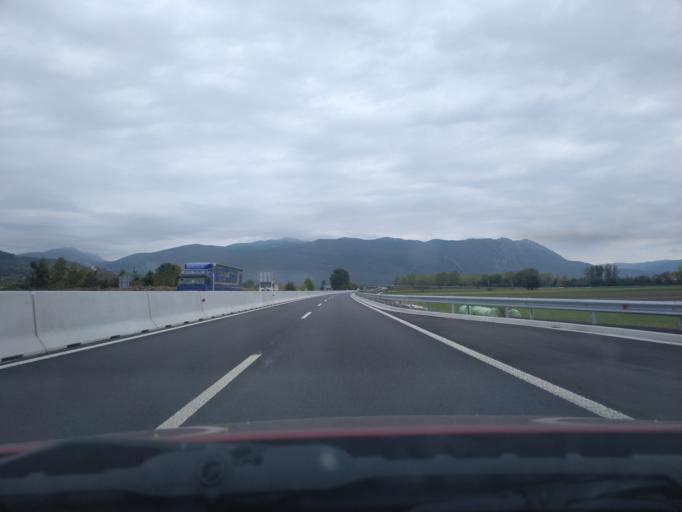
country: SI
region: Ajdovscina
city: Ajdovscina
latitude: 45.8761
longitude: 13.9158
